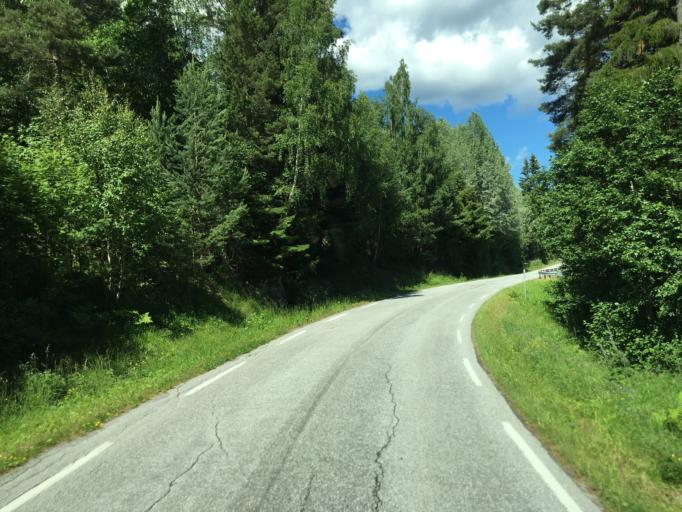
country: NO
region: Oppland
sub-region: Jevnaker
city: Jevnaker
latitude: 60.3528
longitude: 10.3596
